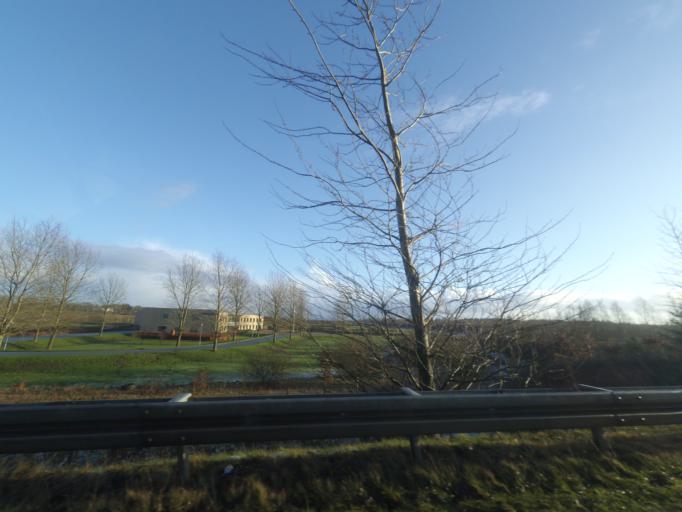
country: DK
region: Central Jutland
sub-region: Ikast-Brande Kommune
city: Ikast
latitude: 56.1207
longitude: 9.1752
